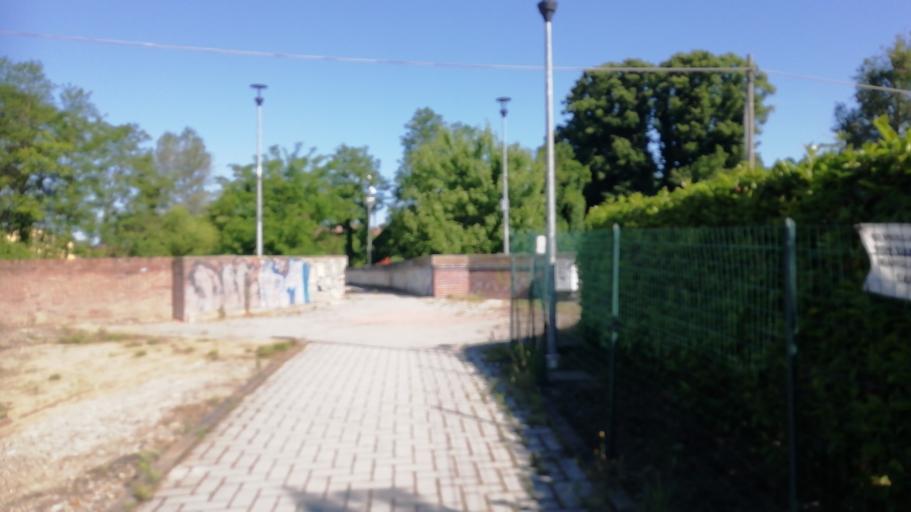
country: IT
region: Emilia-Romagna
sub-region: Provincia di Piacenza
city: Cortemaggiore
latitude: 44.9940
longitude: 9.9375
